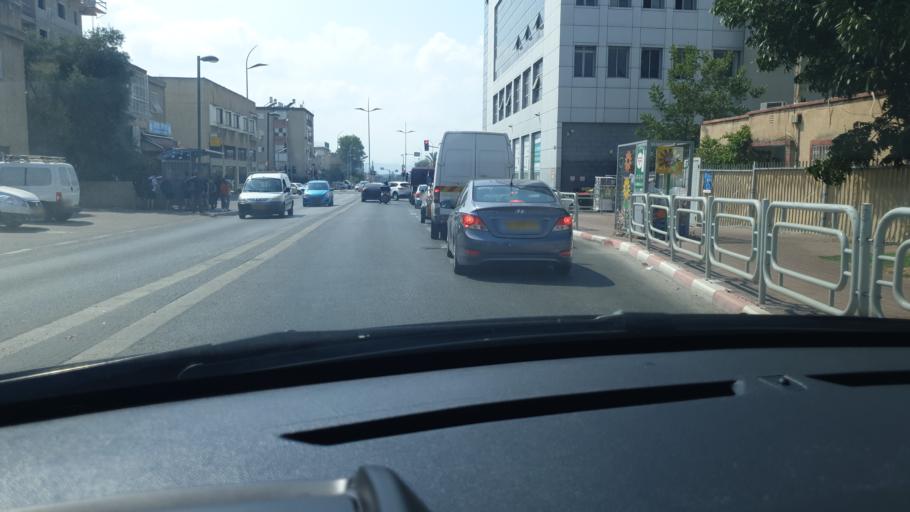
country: IL
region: Haifa
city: Qiryat Ata
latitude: 32.8124
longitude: 35.1061
